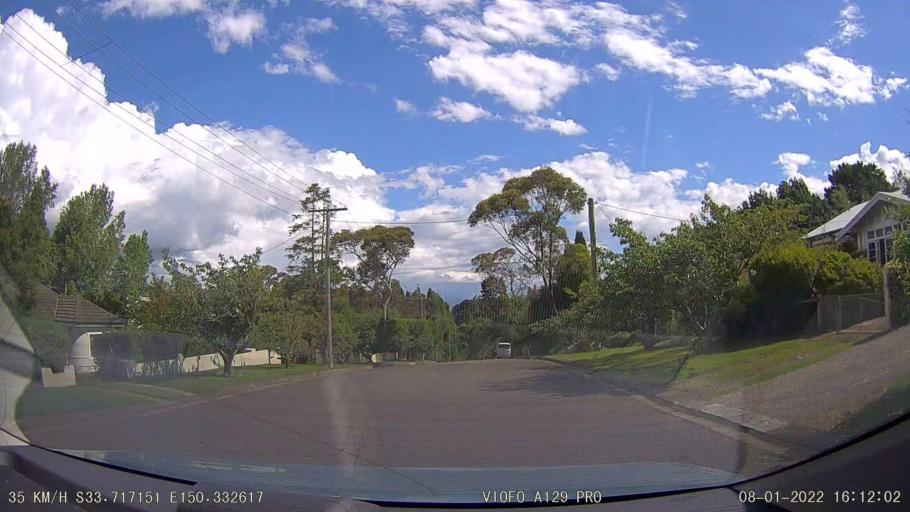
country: AU
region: New South Wales
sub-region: Blue Mountains Municipality
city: Leura
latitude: -33.7171
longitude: 150.3327
